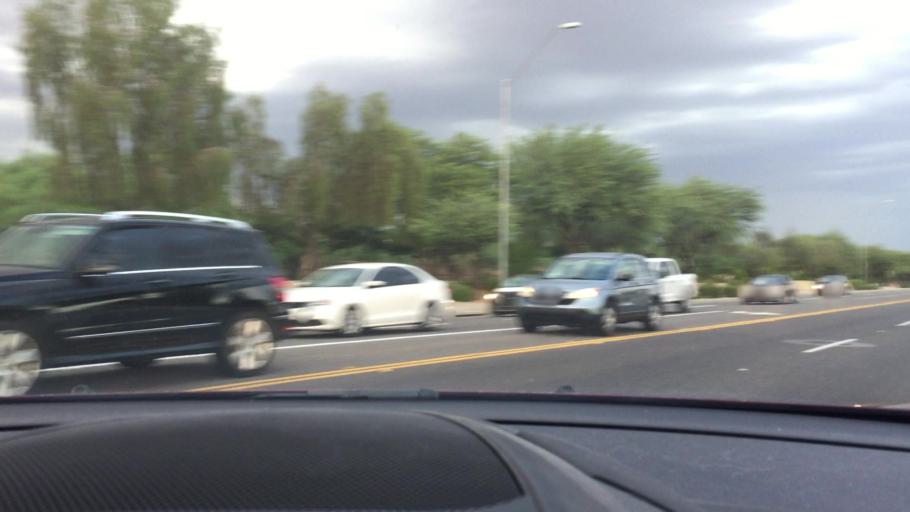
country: US
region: Arizona
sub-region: Maricopa County
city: Sun City
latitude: 33.6672
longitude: -112.2549
